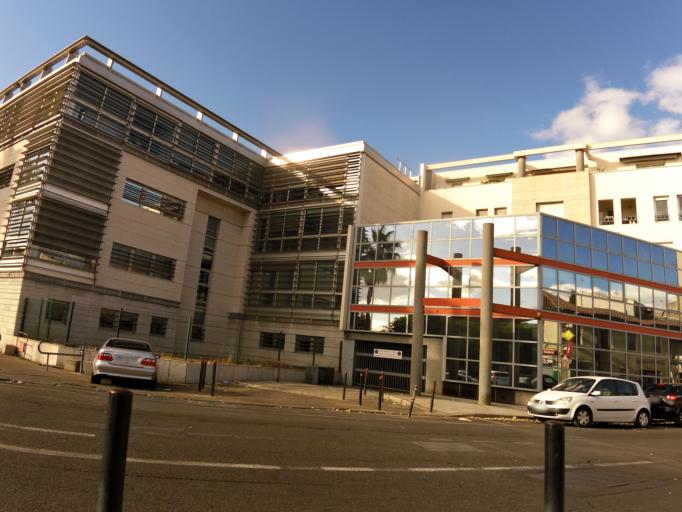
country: FR
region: Languedoc-Roussillon
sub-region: Departement du Gard
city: Nimes
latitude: 43.8403
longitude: 4.3655
